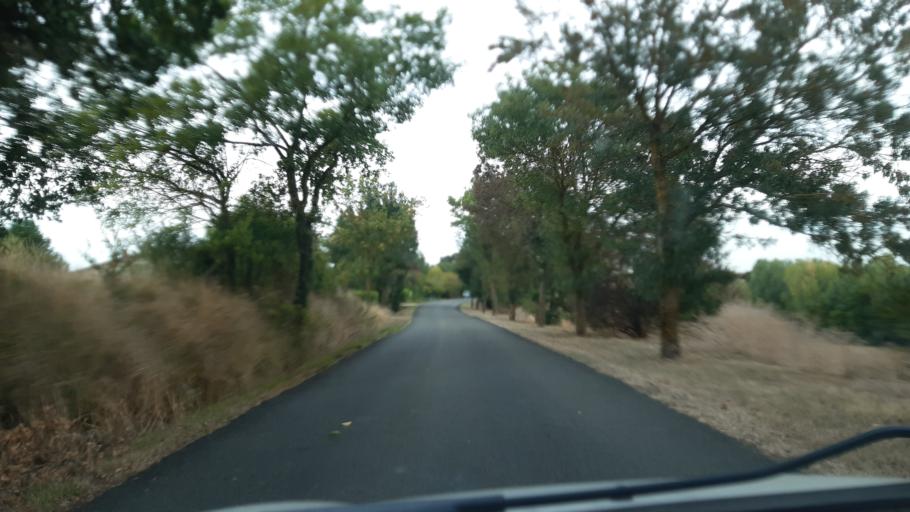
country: FR
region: Midi-Pyrenees
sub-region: Departement du Gers
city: Gimont
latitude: 43.6823
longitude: 0.9991
